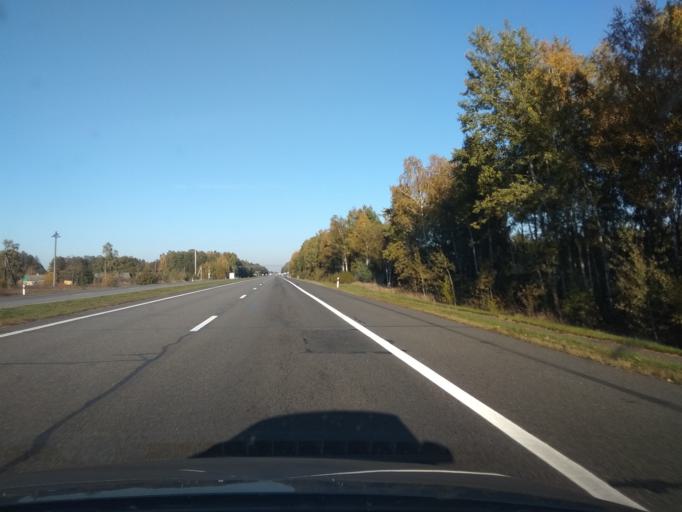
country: BY
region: Brest
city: Ivatsevichy
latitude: 52.6807
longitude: 25.3288
